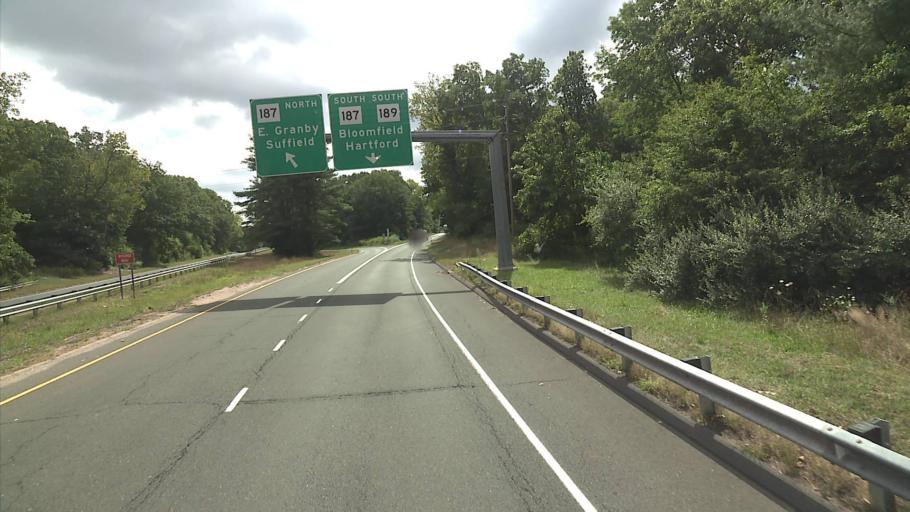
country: US
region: Connecticut
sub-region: Hartford County
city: Tariffville
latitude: 41.8977
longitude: -72.7537
